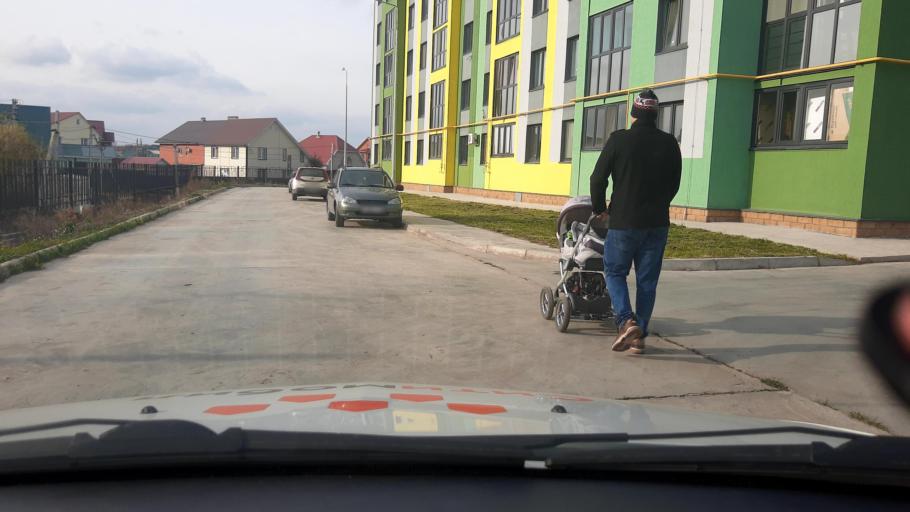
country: RU
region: Bashkortostan
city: Ufa
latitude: 54.7954
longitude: 55.9508
